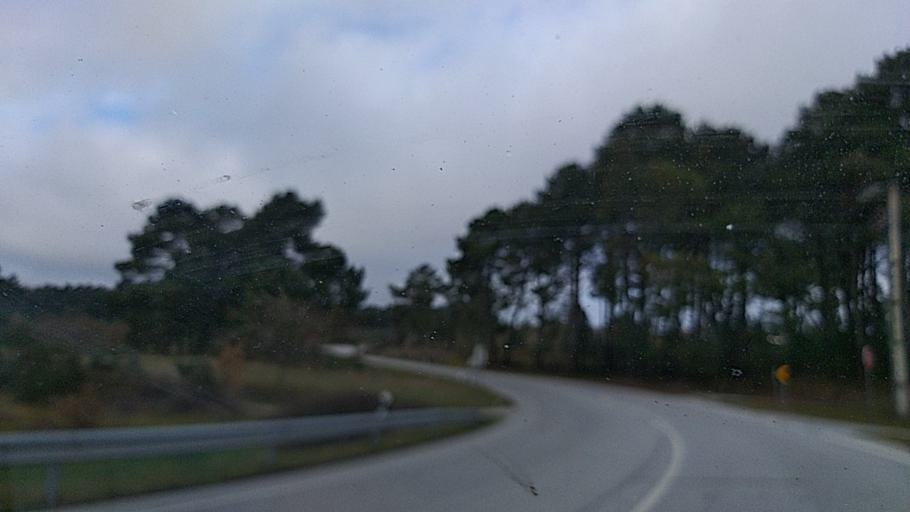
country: PT
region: Guarda
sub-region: Fornos de Algodres
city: Fornos de Algodres
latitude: 40.7191
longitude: -7.4884
